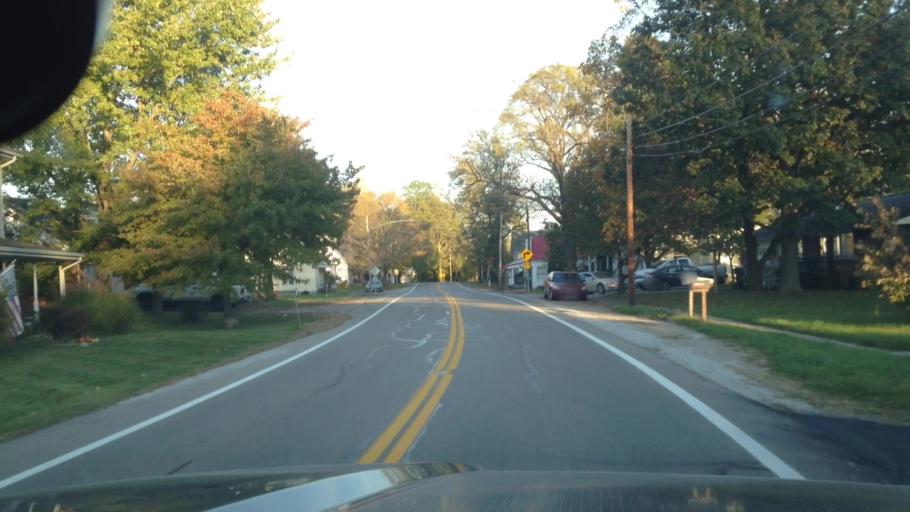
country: US
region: Ohio
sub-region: Butler County
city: Oxford
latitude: 39.5962
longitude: -84.7375
